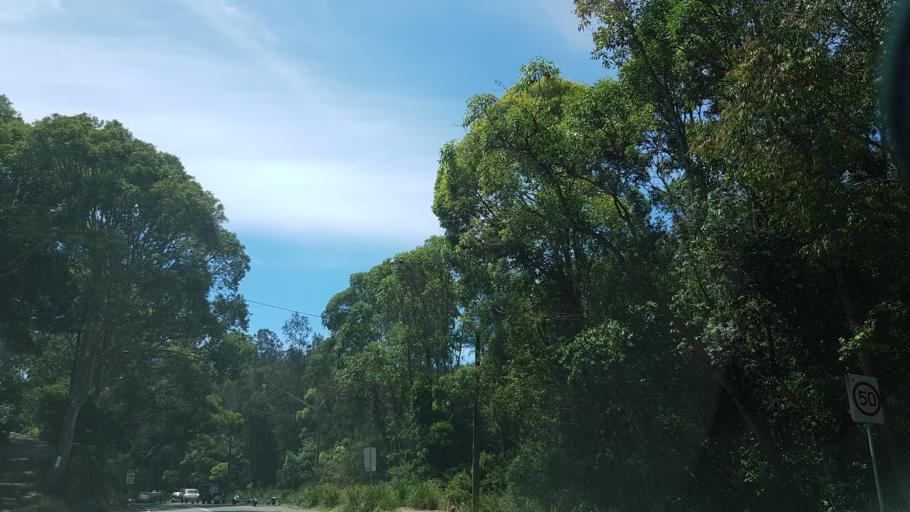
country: AU
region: New South Wales
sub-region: Pittwater
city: Bay View
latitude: -33.6655
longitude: 151.3015
